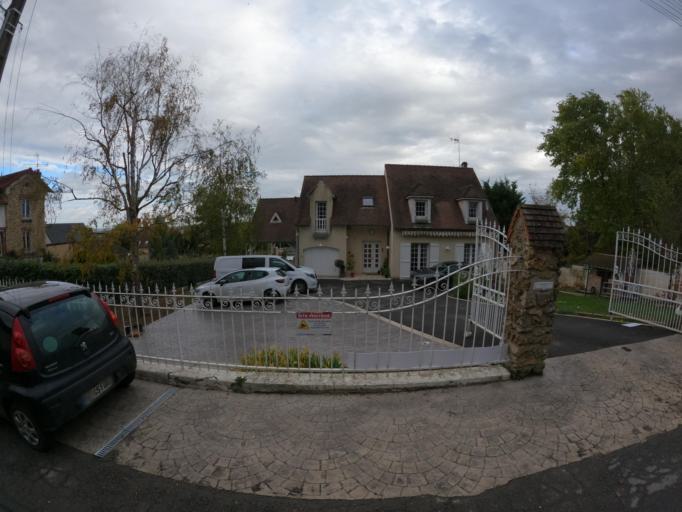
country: FR
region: Ile-de-France
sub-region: Departement de Seine-et-Marne
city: Saint-Germain-sur-Morin
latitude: 48.8744
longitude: 2.8400
